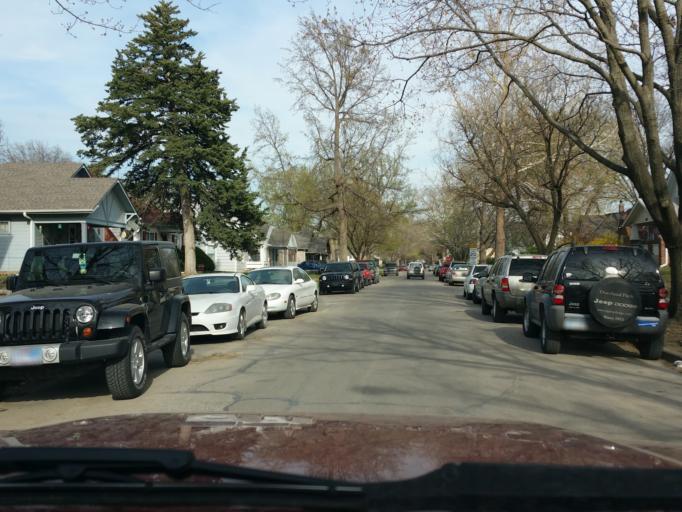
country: US
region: Kansas
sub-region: Riley County
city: Manhattan
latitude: 39.1879
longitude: -96.5698
